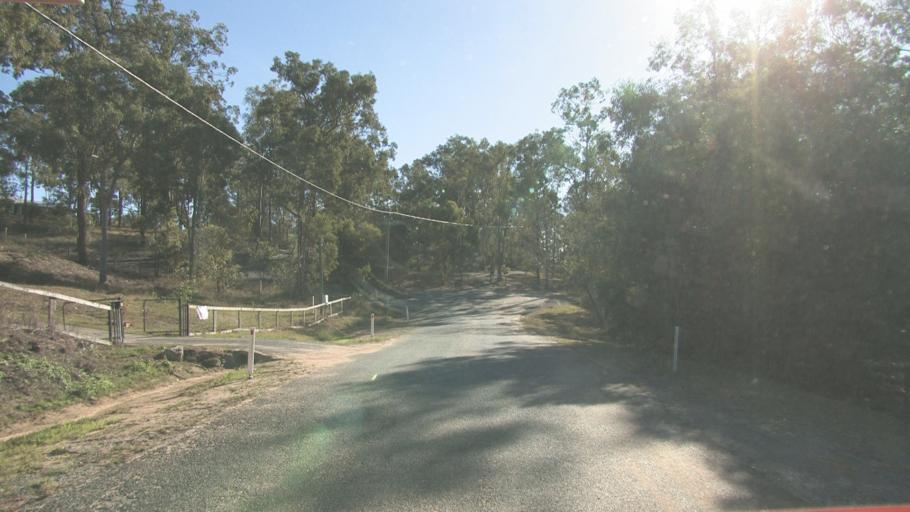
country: AU
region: Queensland
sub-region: Ipswich
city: Springfield Lakes
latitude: -27.6996
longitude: 152.9264
